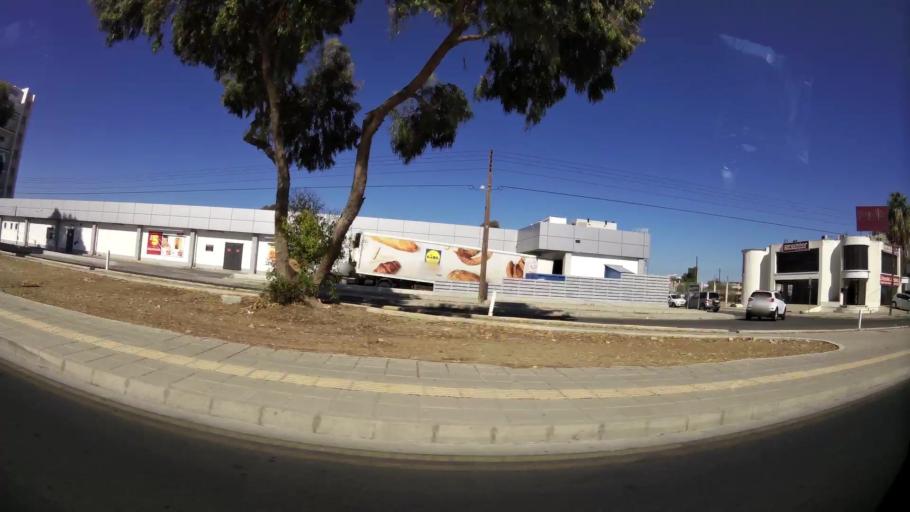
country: CY
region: Larnaka
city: Larnaca
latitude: 34.9351
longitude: 33.6397
